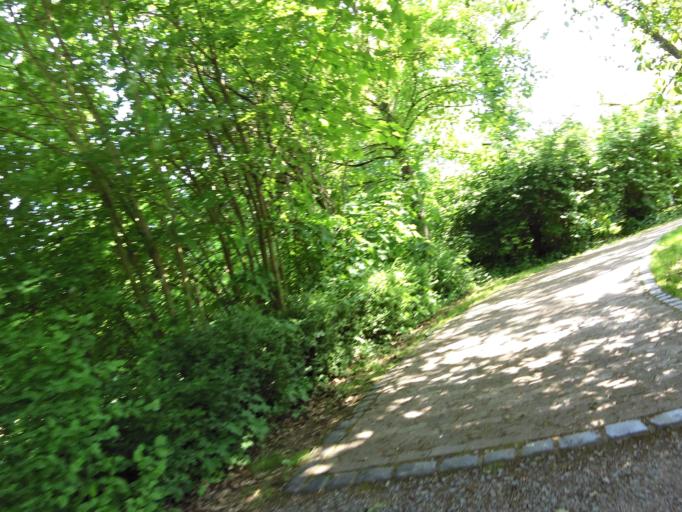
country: DE
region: Bavaria
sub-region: Regierungsbezirk Unterfranken
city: Wuerzburg
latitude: 49.7768
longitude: 9.9523
